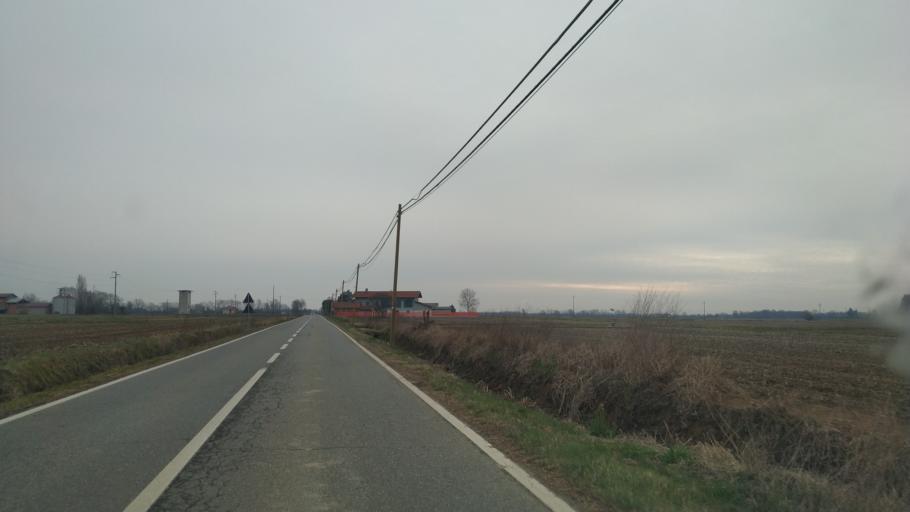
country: IT
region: Piedmont
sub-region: Provincia di Vercelli
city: San Giacomo Vercellese
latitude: 45.4934
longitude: 8.2982
